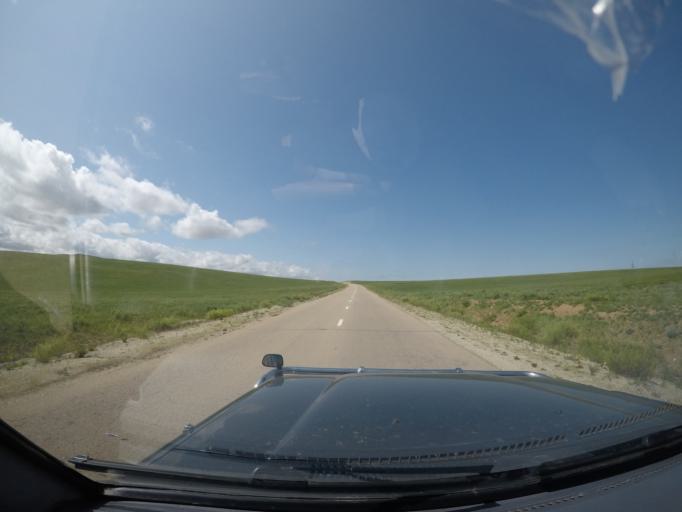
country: MN
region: Hentiy
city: Bayan
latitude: 47.2883
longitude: 111.1176
